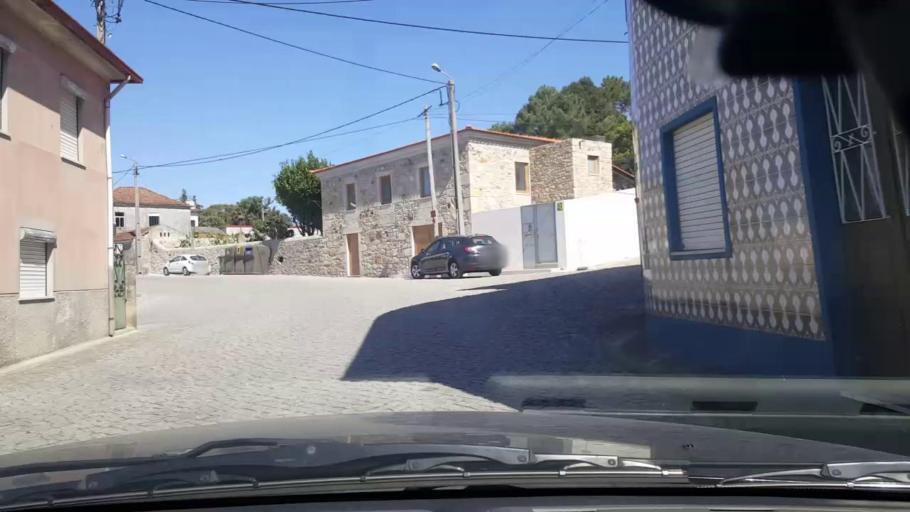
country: PT
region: Porto
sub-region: Maia
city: Gemunde
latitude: 41.3302
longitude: -8.6441
